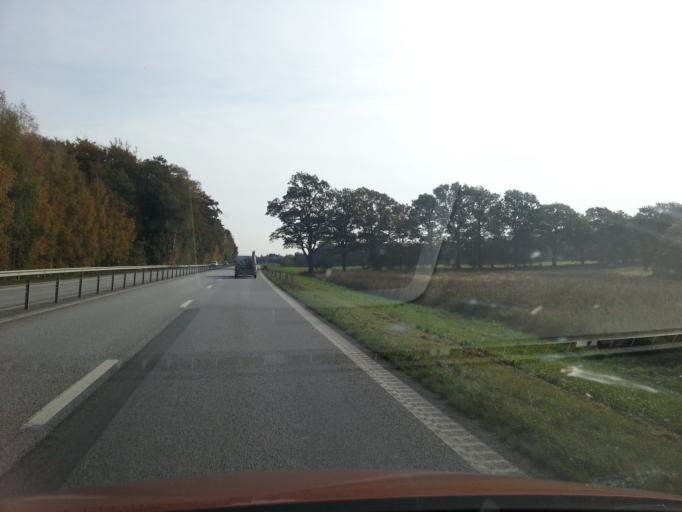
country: SE
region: Skane
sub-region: Lunds Kommun
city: Veberod
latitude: 55.6514
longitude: 13.4478
